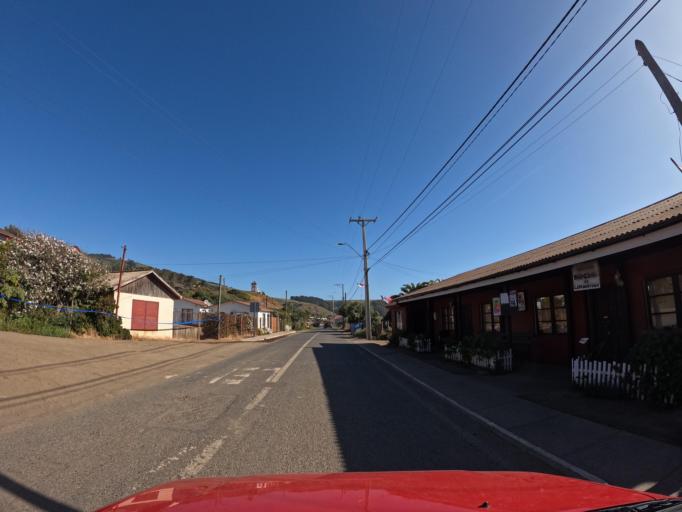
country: CL
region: Maule
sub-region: Provincia de Talca
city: Constitucion
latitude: -34.8500
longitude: -72.1415
